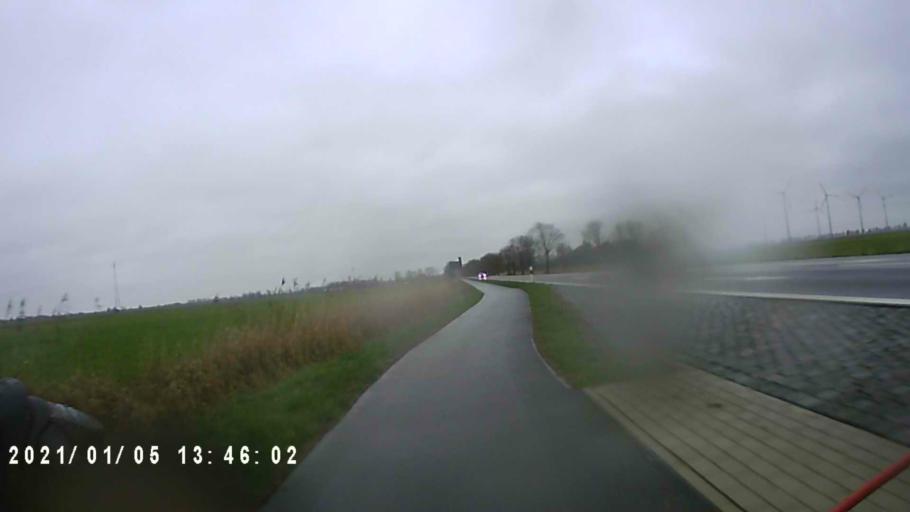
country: DE
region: Lower Saxony
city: Weener
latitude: 53.1867
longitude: 7.3842
